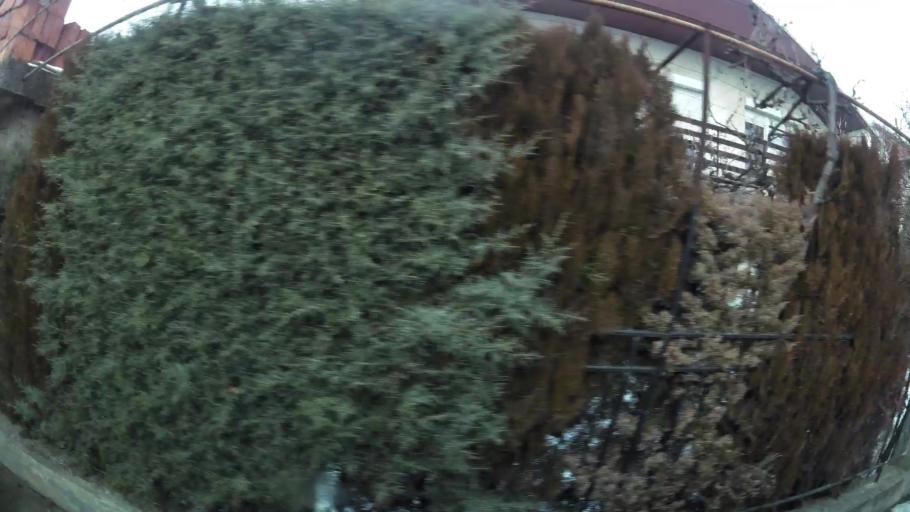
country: MK
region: Saraj
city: Saraj
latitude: 42.0248
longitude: 21.3547
